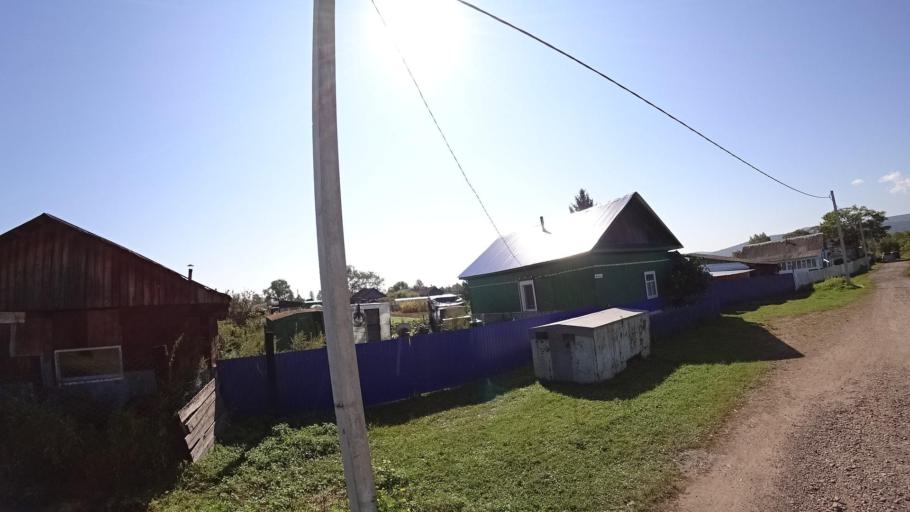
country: RU
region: Jewish Autonomous Oblast
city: Bira
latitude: 48.9979
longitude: 132.4499
